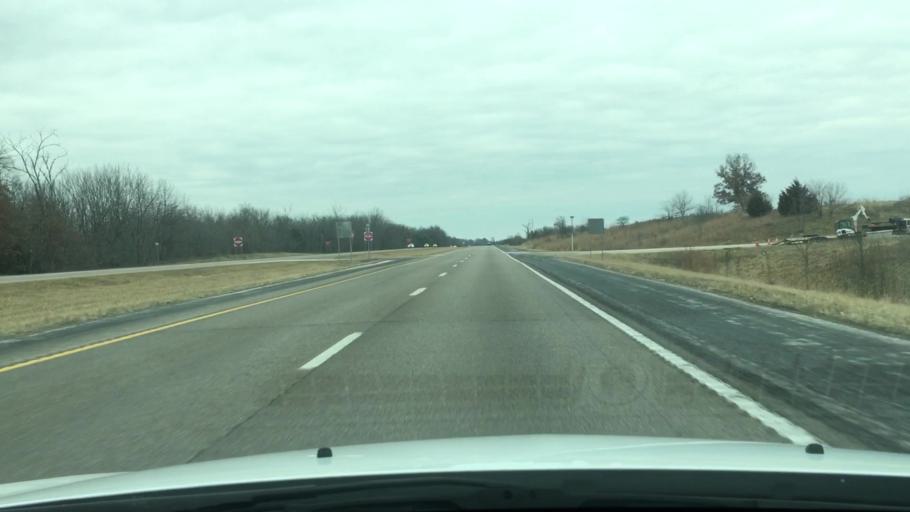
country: US
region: Missouri
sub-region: Callaway County
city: Fulton
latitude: 38.9881
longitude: -91.8938
